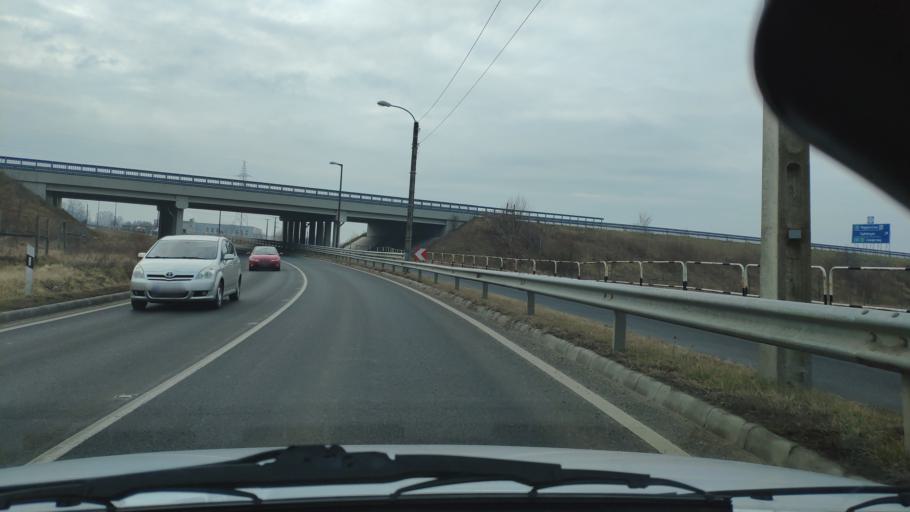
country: HU
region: Zala
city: Nagykanizsa
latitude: 46.4789
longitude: 16.9849
